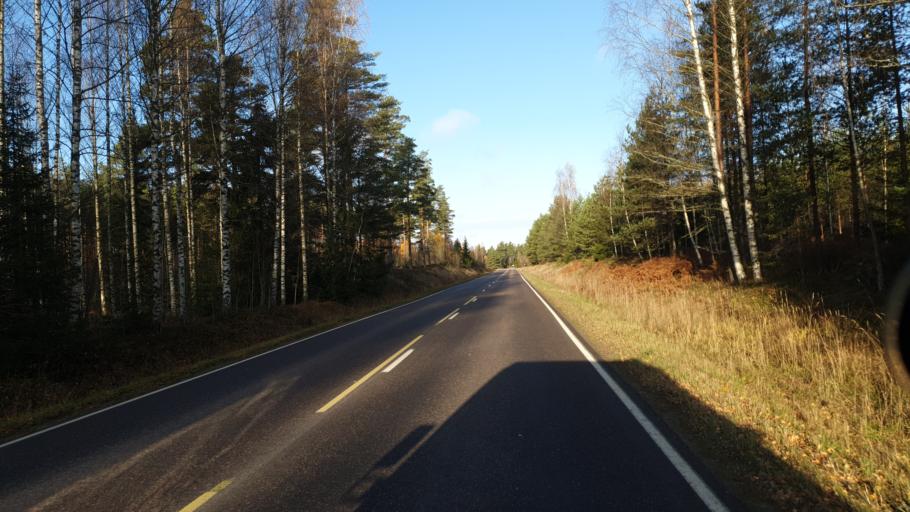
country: FI
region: Uusimaa
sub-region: Helsinki
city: Siuntio
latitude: 60.1949
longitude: 24.1952
